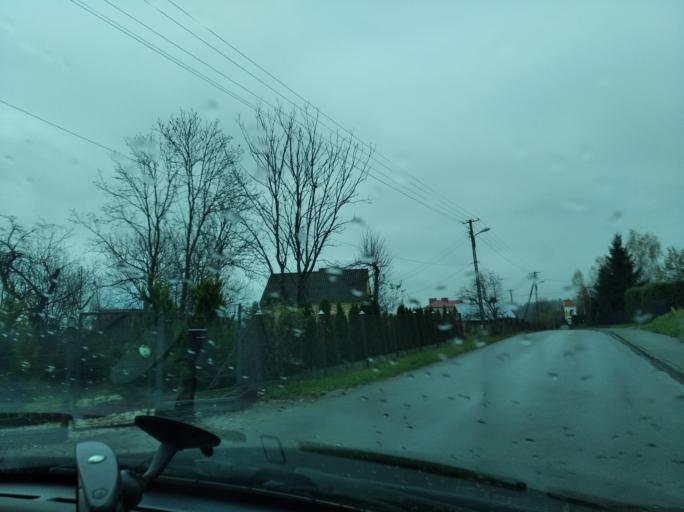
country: PL
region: Subcarpathian Voivodeship
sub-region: Powiat rzeszowski
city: Tyczyn
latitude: 49.9593
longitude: 22.0373
